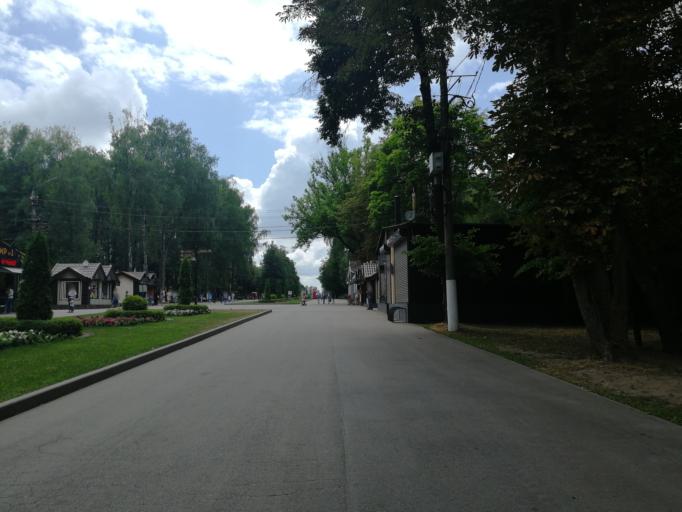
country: RU
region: Tula
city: Tula
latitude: 54.1825
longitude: 37.5914
